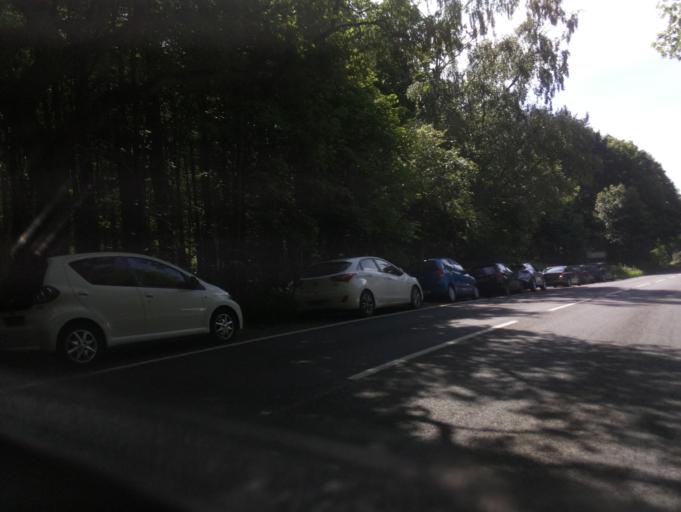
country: GB
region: England
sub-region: North Lincolnshire
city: Manton
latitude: 53.5405
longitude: -0.5768
